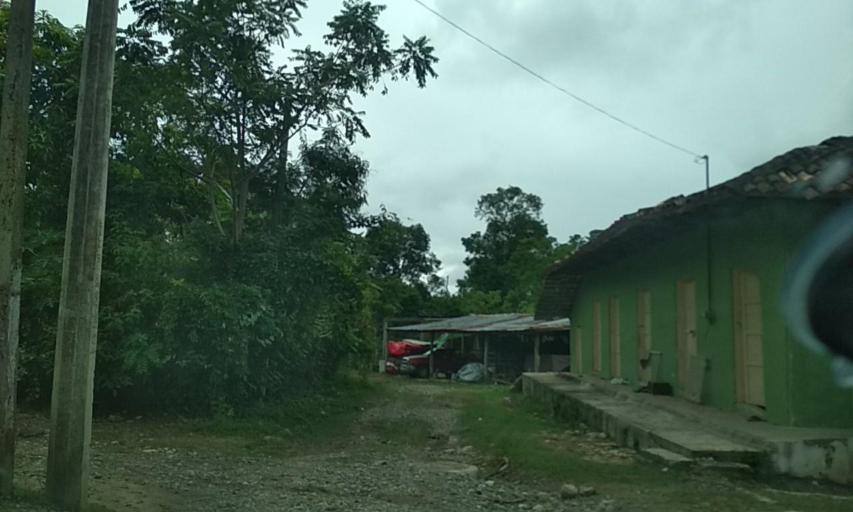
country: MX
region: Veracruz
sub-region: Papantla
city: Residencial Tajin
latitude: 20.6000
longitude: -97.3348
